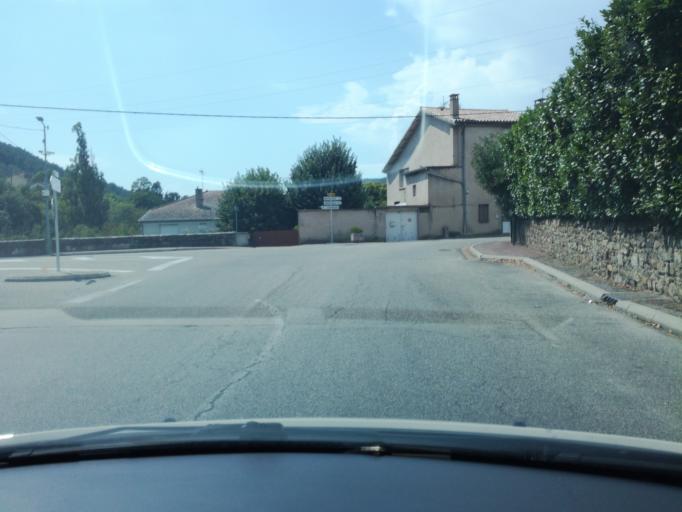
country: FR
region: Rhone-Alpes
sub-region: Departement de l'Ardeche
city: Labegude
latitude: 44.6376
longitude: 4.3744
